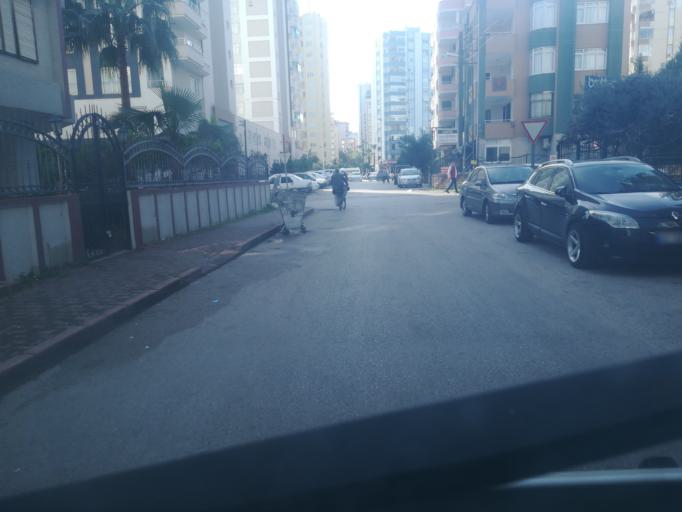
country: TR
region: Adana
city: Adana
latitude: 37.0404
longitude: 35.3162
